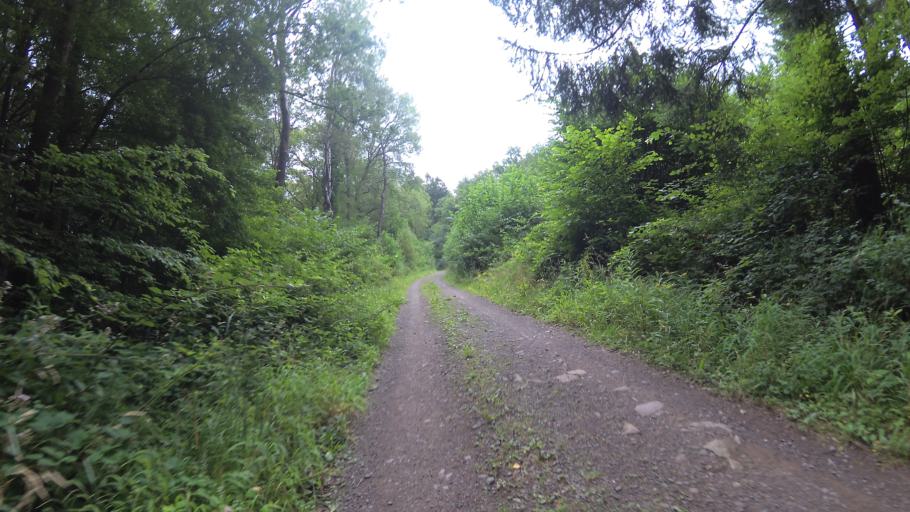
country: DE
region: Saarland
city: Mainzweiler
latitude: 49.4209
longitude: 7.1430
